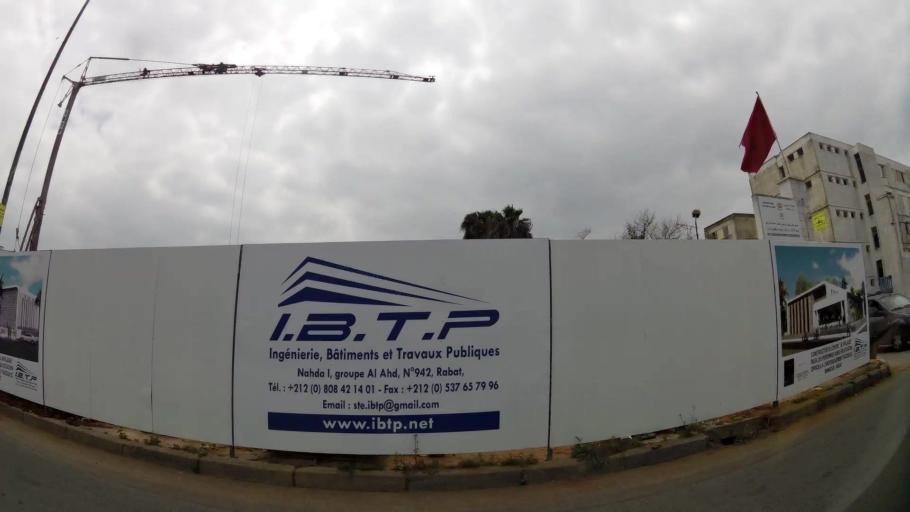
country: MA
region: Rabat-Sale-Zemmour-Zaer
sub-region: Rabat
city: Rabat
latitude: 33.9979
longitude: -6.8656
